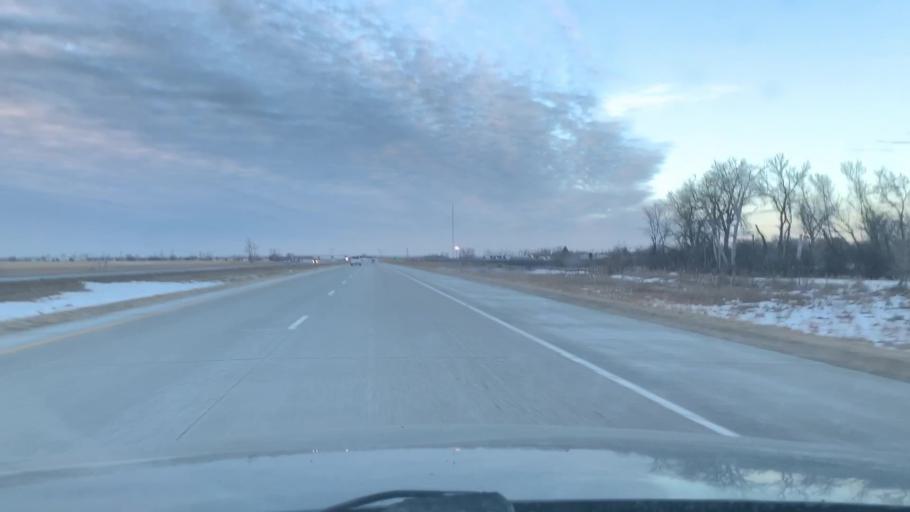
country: US
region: North Dakota
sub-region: Barnes County
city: Valley City
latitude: 46.9115
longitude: -97.6711
